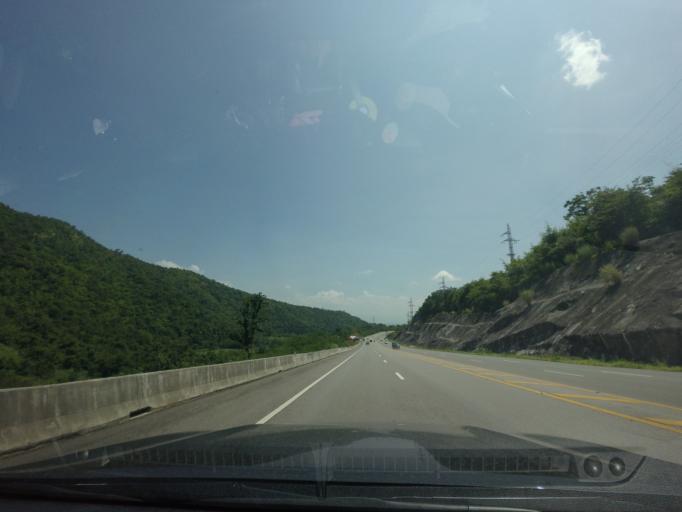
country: TH
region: Phetchabun
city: Lom Sak
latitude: 16.7728
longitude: 101.1327
